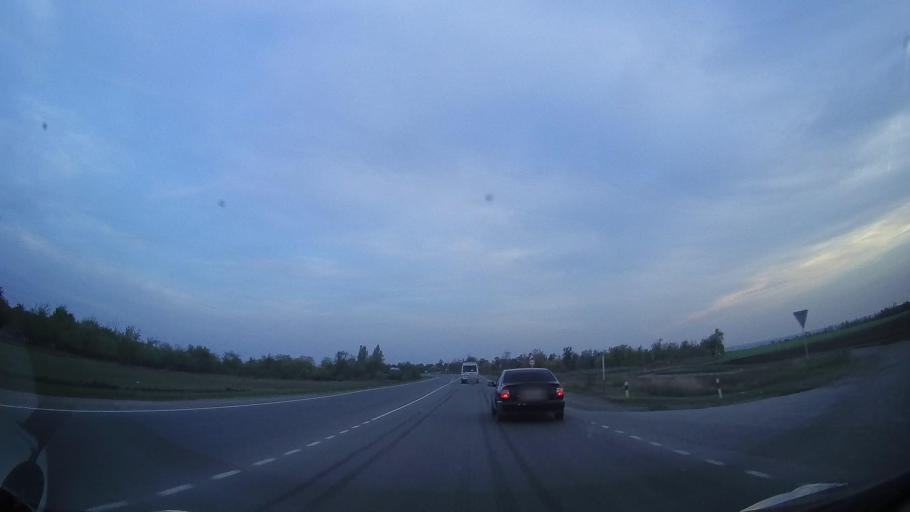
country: RU
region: Rostov
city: Kagal'nitskaya
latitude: 46.8927
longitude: 40.1298
